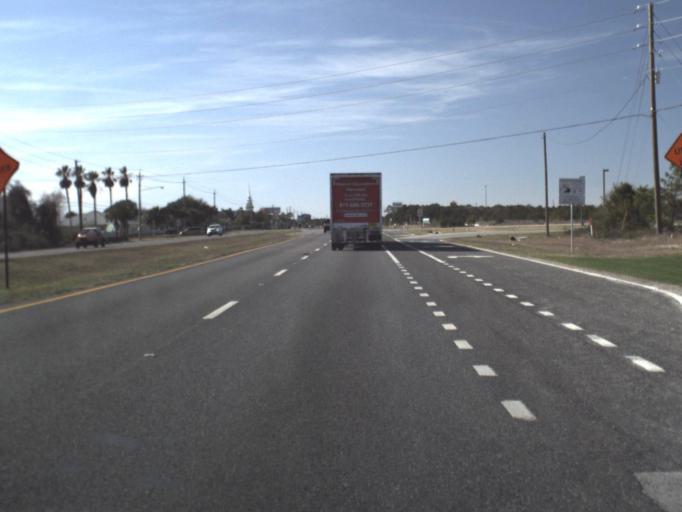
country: US
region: Florida
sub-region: Bay County
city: Laguna Beach
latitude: 30.2327
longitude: -85.8949
